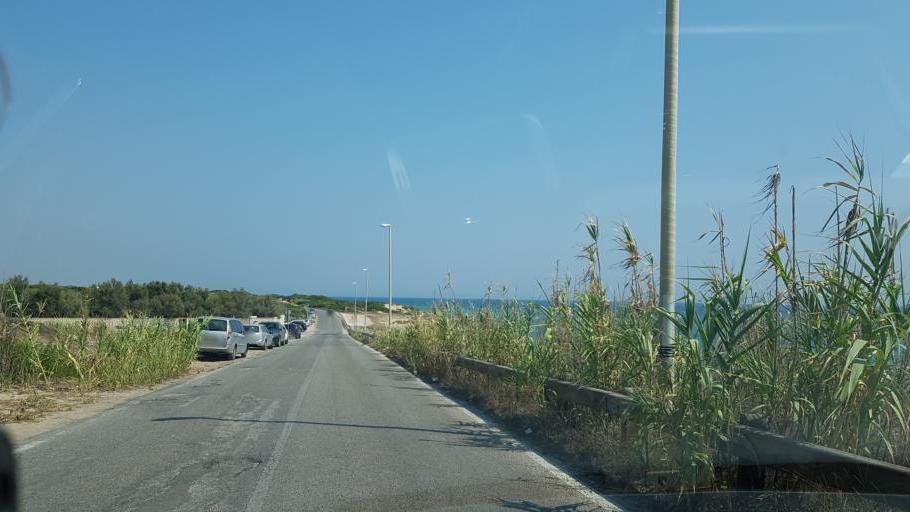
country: IT
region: Apulia
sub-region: Provincia di Taranto
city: Maruggio
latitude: 40.3000
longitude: 17.5799
